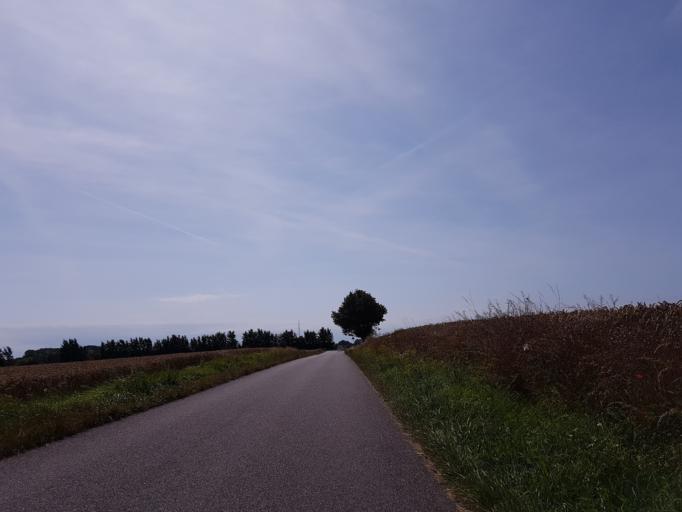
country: DK
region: Zealand
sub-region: Guldborgsund Kommune
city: Nykobing Falster
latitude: 54.5877
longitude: 11.9409
